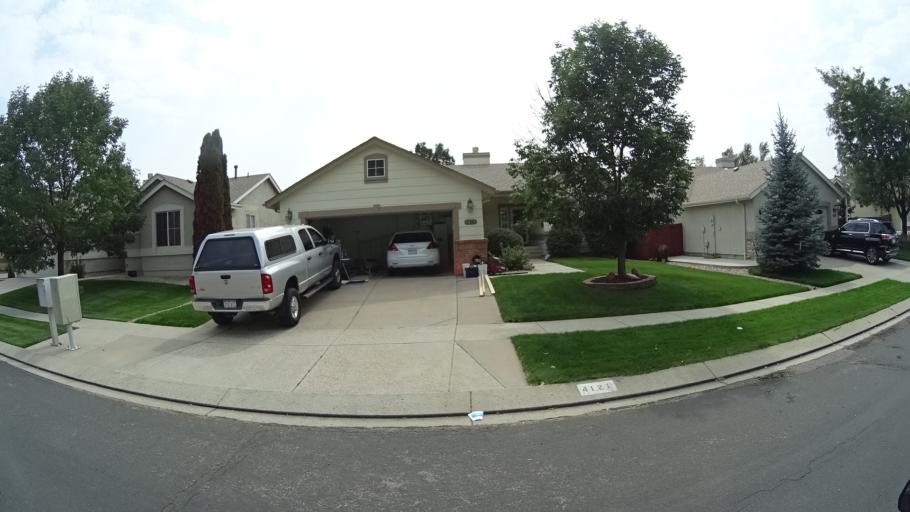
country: US
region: Colorado
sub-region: El Paso County
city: Cimarron Hills
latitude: 38.8233
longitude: -104.7385
